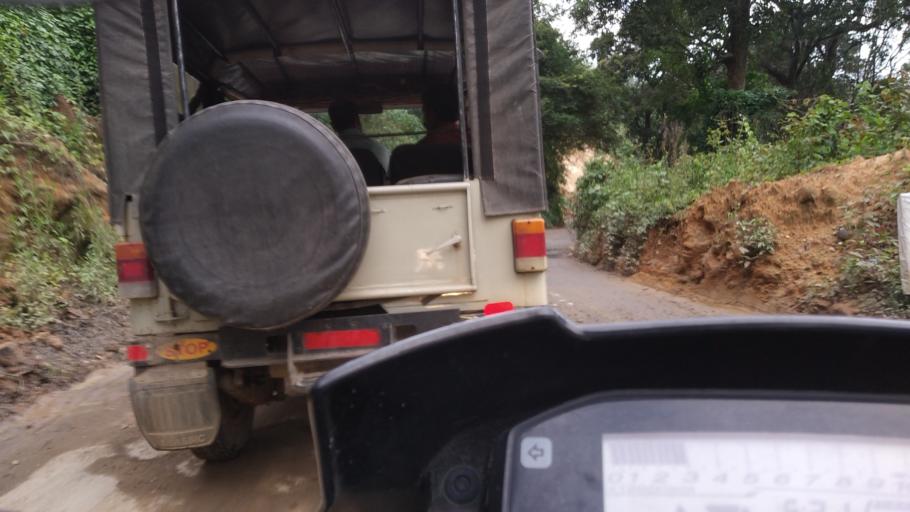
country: IN
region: Tamil Nadu
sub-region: Theni
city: Bodinayakkanur
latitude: 10.0175
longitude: 77.2429
